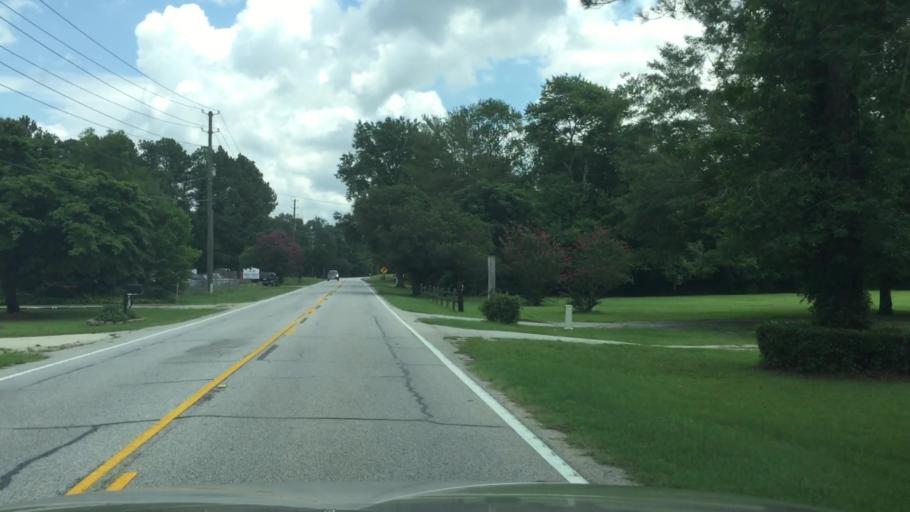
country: US
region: South Carolina
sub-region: Sumter County
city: South Sumter
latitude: 33.9122
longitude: -80.3979
